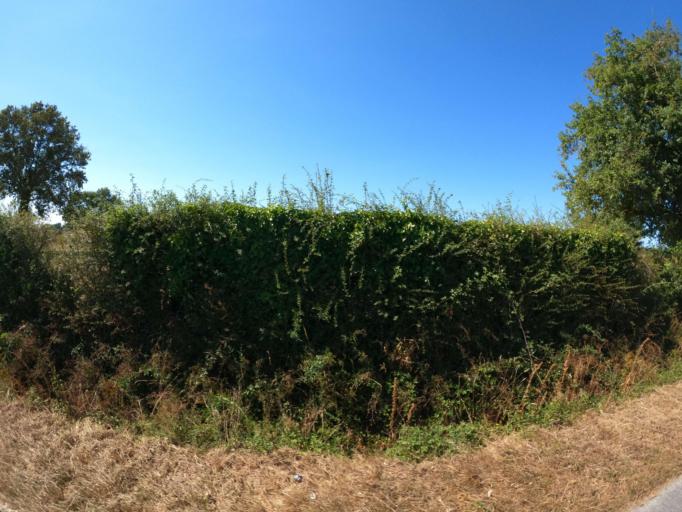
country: FR
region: Pays de la Loire
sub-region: Departement de la Vendee
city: Saint-Aubin-des-Ormeaux
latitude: 47.0069
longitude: -1.0057
